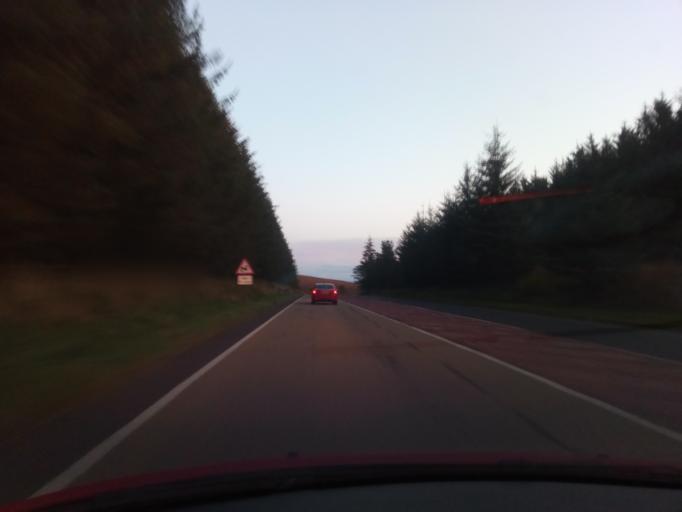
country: GB
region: Scotland
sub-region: East Lothian
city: Pencaitland
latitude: 55.8072
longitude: -2.8367
